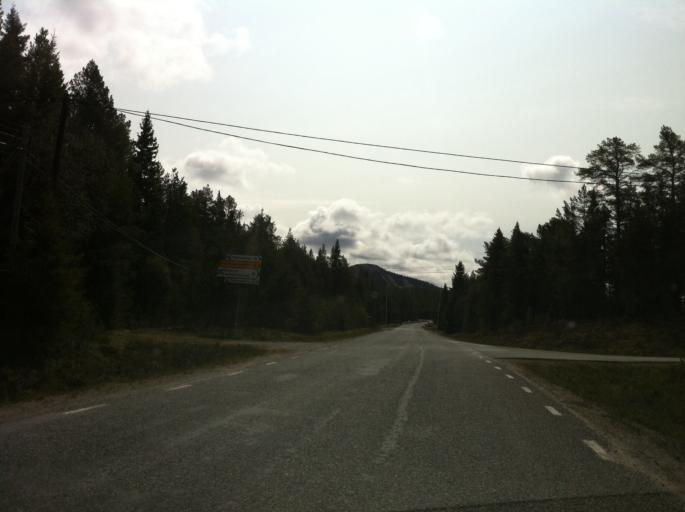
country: NO
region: Hedmark
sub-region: Engerdal
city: Engerdal
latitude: 62.4399
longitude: 12.6809
